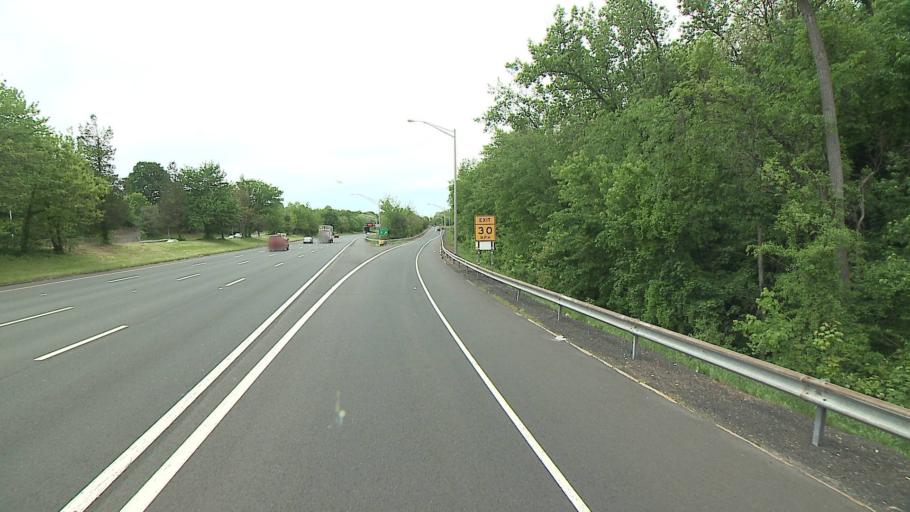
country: US
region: Connecticut
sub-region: Hartford County
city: Manchester
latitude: 41.7632
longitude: -72.5362
